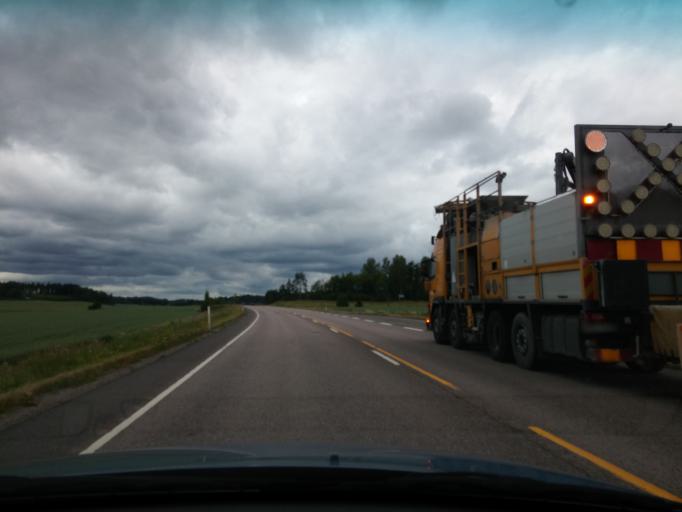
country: FI
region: Uusimaa
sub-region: Porvoo
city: Askola
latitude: 60.4760
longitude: 25.5680
